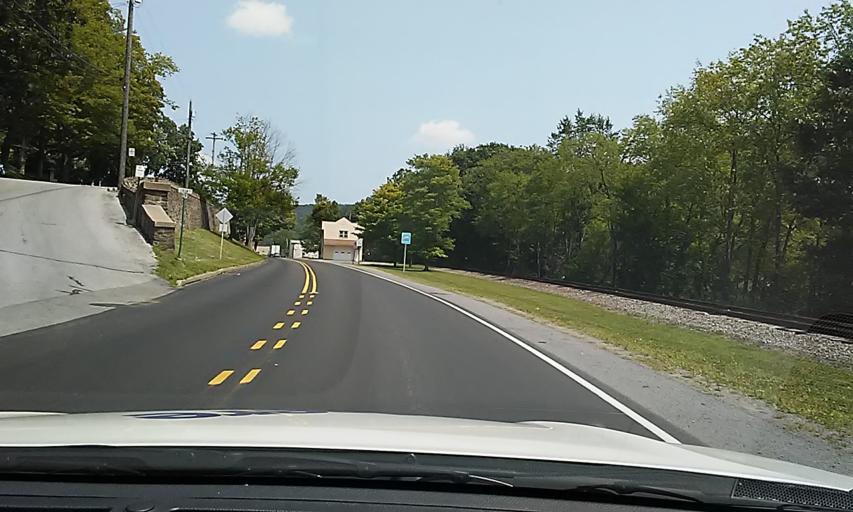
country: US
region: Pennsylvania
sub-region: Elk County
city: Ridgway
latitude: 41.4263
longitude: -78.7261
